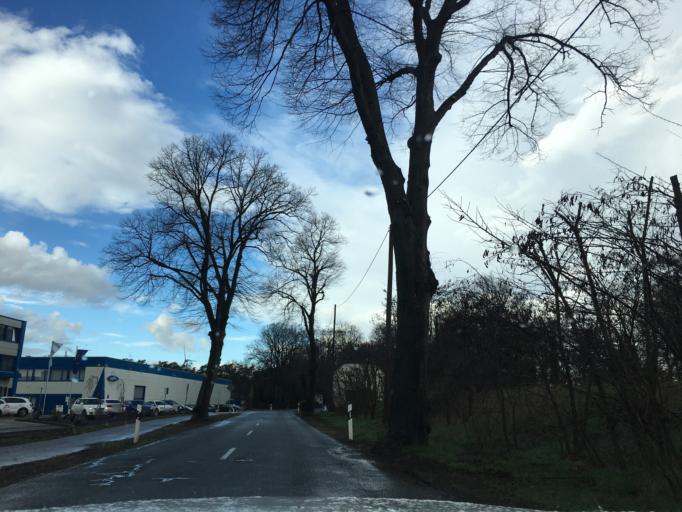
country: DE
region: North Rhine-Westphalia
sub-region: Regierungsbezirk Munster
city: Isselburg
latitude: 51.7829
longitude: 6.4653
